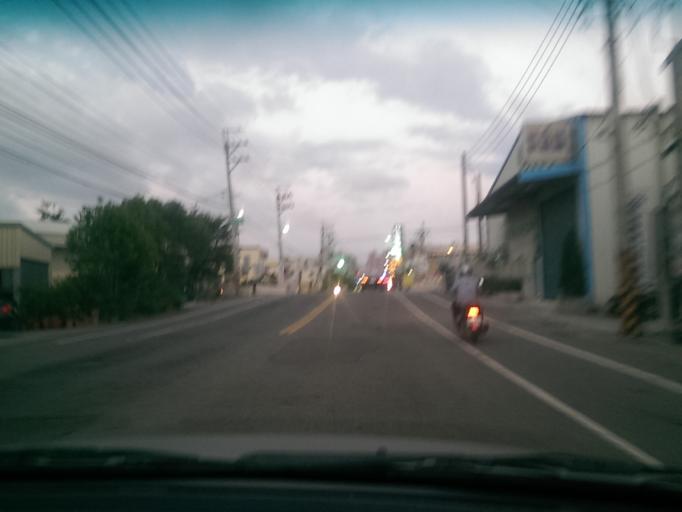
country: TW
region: Taiwan
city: Fengyuan
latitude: 24.2190
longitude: 120.6402
